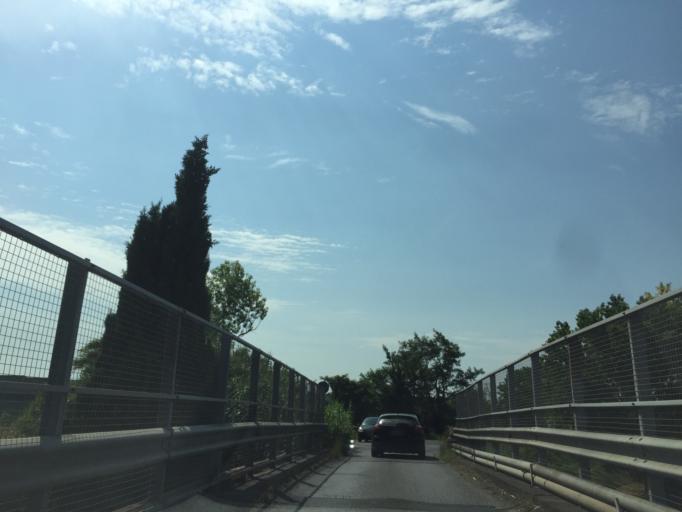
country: IT
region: Tuscany
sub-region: Provincia di Pistoia
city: Margine Coperta-Traversagna
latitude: 43.8642
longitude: 10.7532
